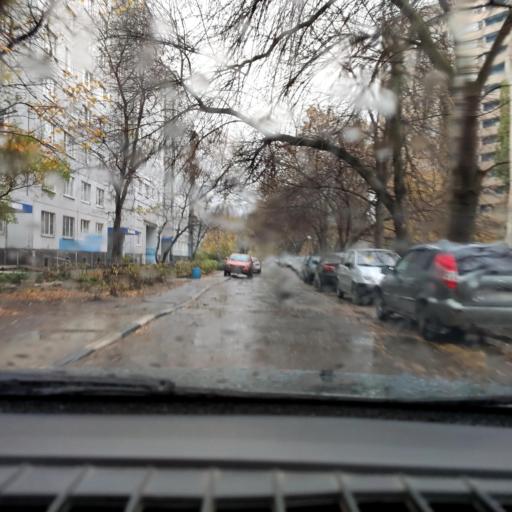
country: RU
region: Samara
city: Tol'yatti
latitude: 53.5314
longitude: 49.3065
